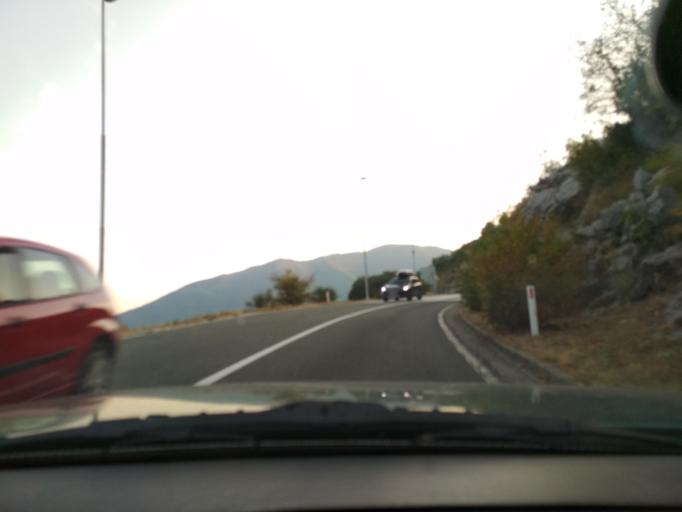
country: ME
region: Kotor
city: Risan
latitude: 42.5145
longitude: 18.6827
